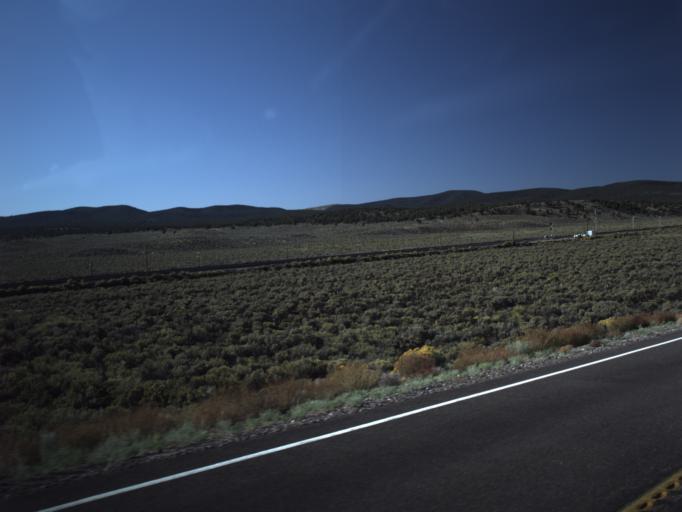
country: US
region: Utah
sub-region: Washington County
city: Enterprise
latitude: 37.7282
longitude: -114.0317
